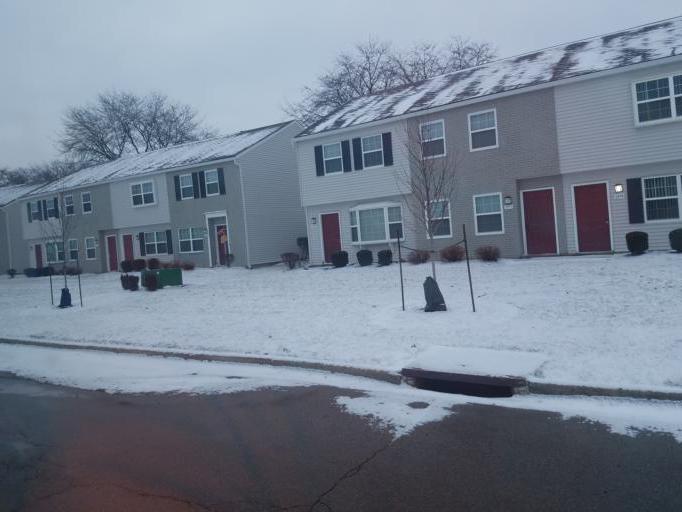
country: US
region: Ohio
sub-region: Franklin County
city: Dublin
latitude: 40.1138
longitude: -83.0856
